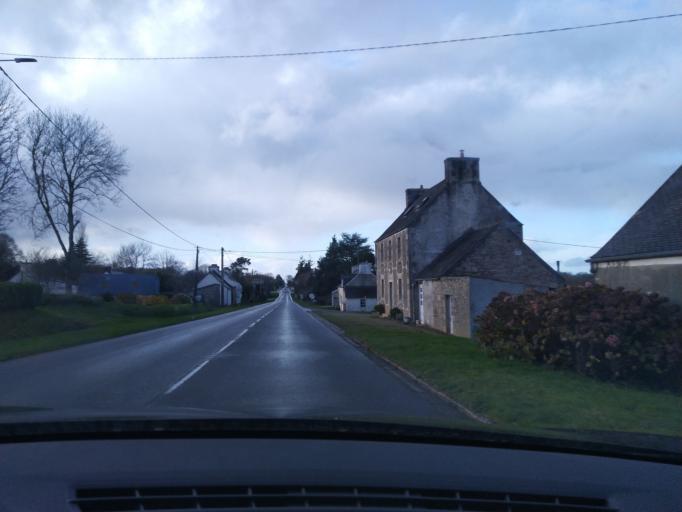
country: FR
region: Brittany
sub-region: Departement du Finistere
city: Guerlesquin
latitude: 48.5674
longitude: -3.6005
